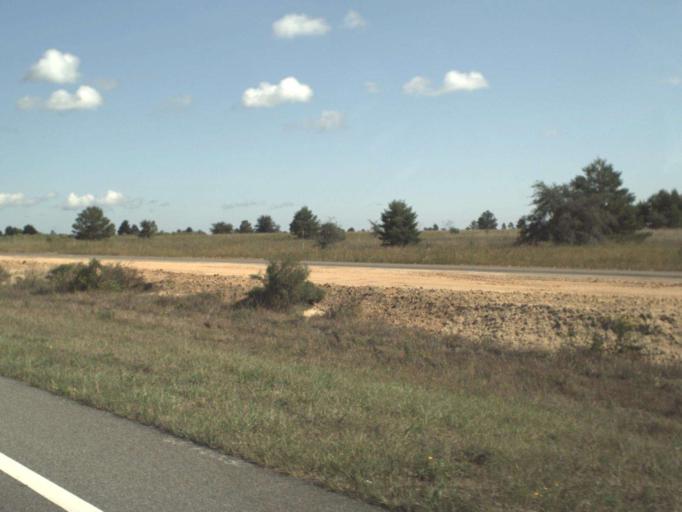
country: US
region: Florida
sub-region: Walton County
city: Freeport
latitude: 30.5360
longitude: -86.1077
